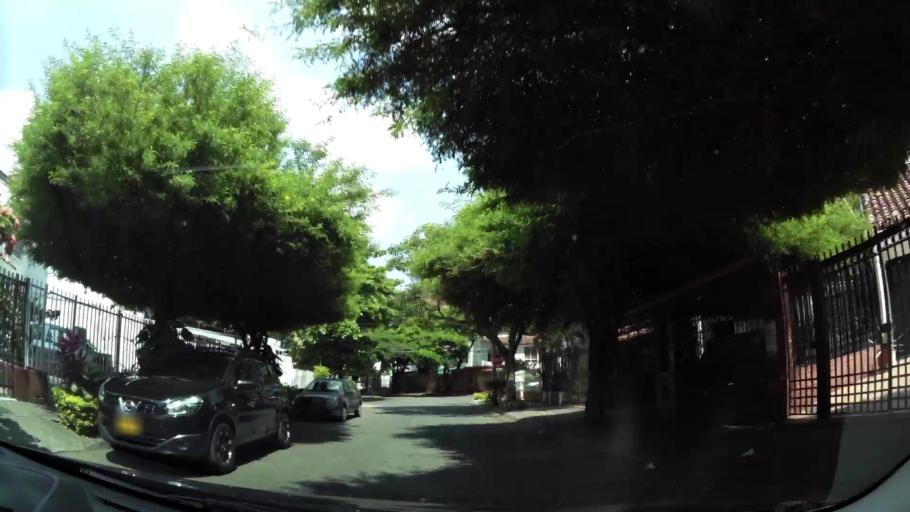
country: CO
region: Valle del Cauca
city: Cali
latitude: 3.4108
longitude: -76.5446
